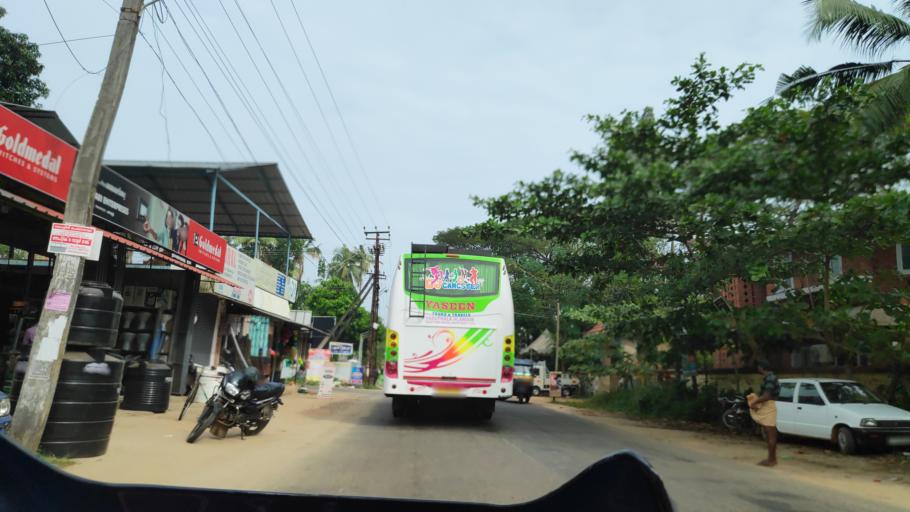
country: IN
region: Kerala
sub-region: Alappuzha
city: Kutiatodu
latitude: 9.8166
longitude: 76.3512
